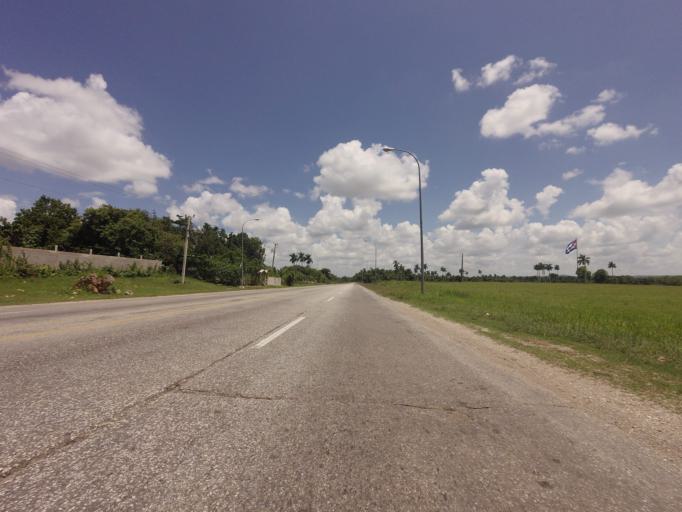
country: CU
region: La Habana
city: Arroyo Naranjo
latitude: 23.0384
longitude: -82.3568
